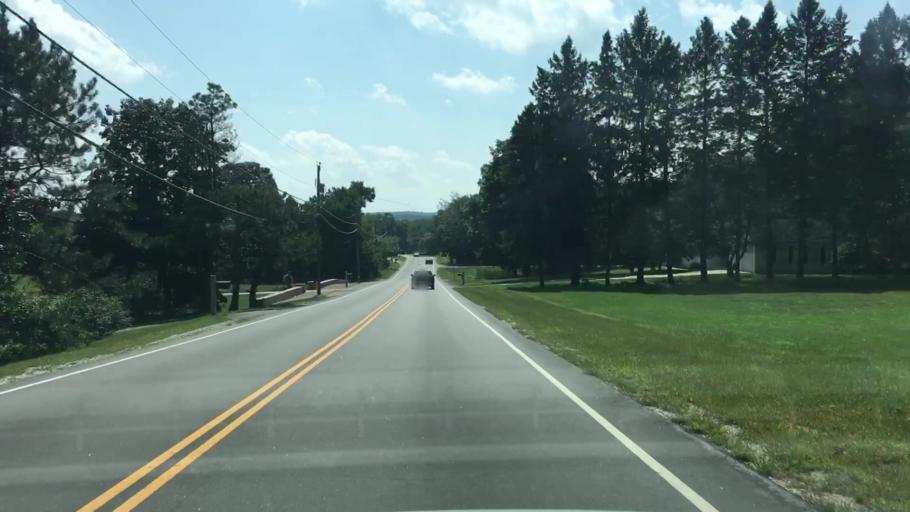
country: US
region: New Hampshire
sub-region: Rockingham County
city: Windham
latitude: 42.7949
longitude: -71.3549
